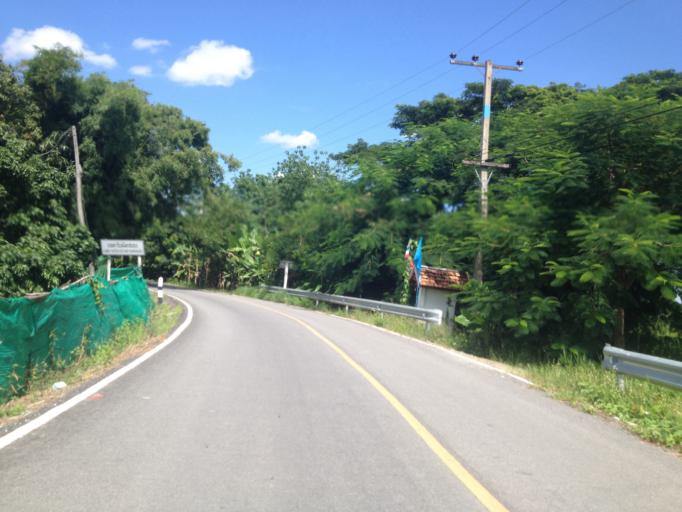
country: TH
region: Chiang Mai
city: Hang Dong
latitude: 18.6613
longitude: 98.9639
